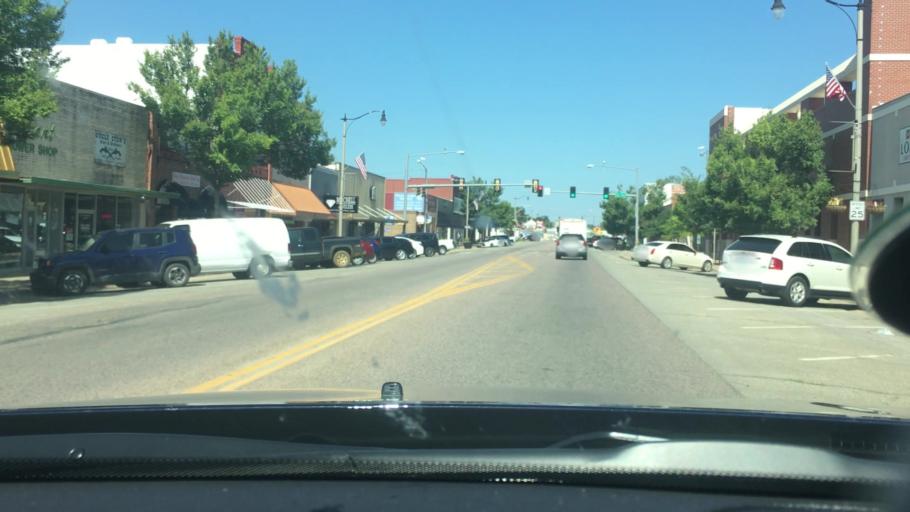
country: US
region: Oklahoma
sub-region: Bryan County
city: Durant
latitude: 33.9911
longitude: -96.3777
